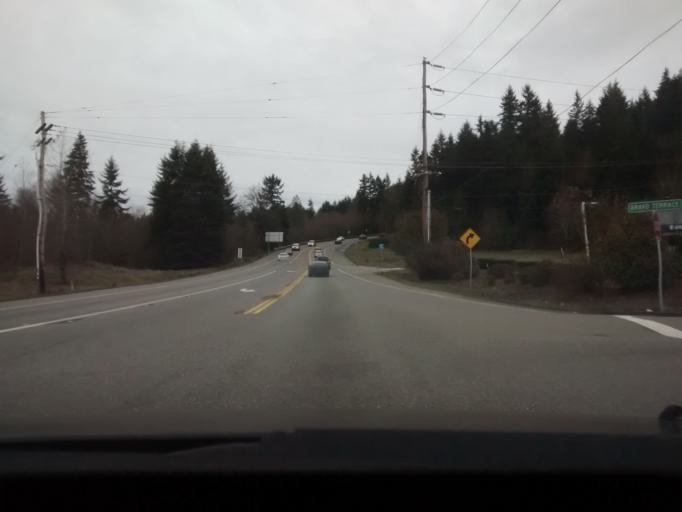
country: US
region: Washington
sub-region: Kitsap County
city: Bethel
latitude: 47.5028
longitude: -122.6440
